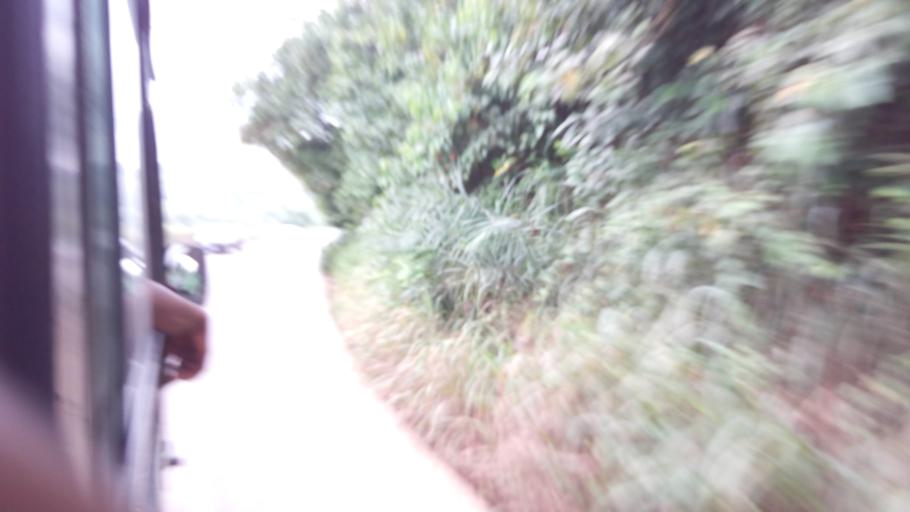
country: CI
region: Lagunes
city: Abidjan
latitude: 5.3378
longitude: -4.1211
